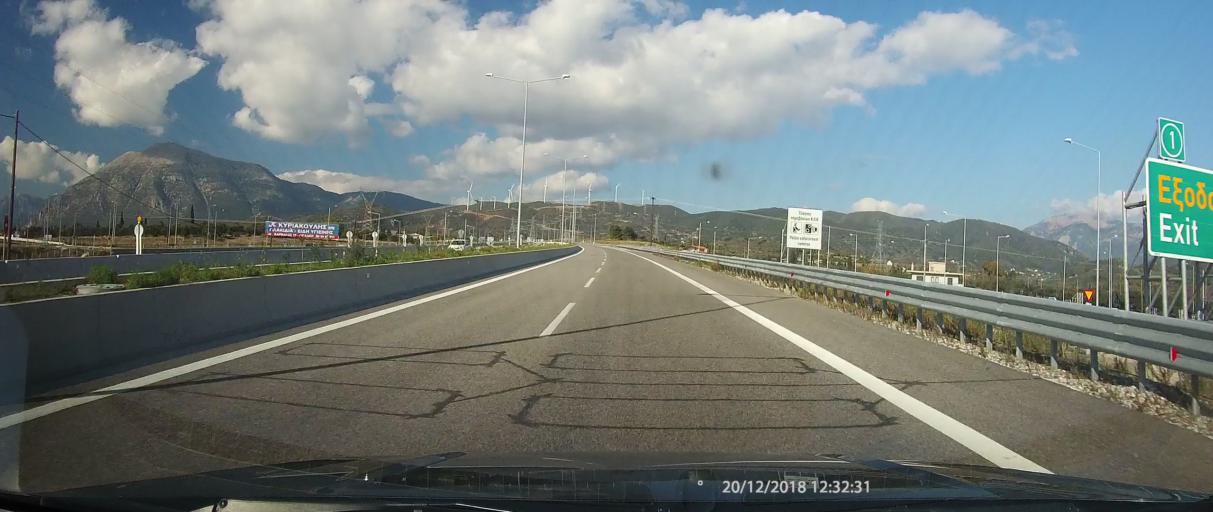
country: GR
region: West Greece
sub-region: Nomos Aitolias kai Akarnanias
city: Antirrio
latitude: 38.3394
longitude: 21.7626
